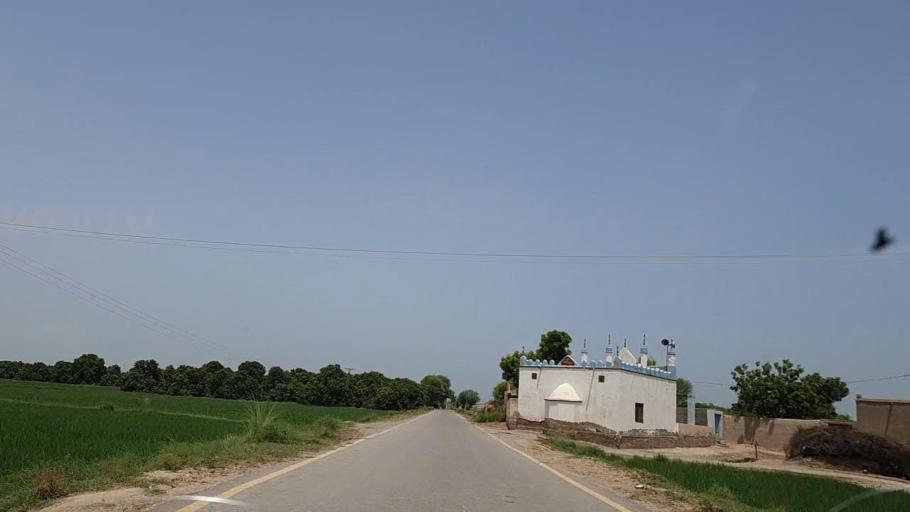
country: PK
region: Sindh
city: Tharu Shah
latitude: 26.9871
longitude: 68.0792
